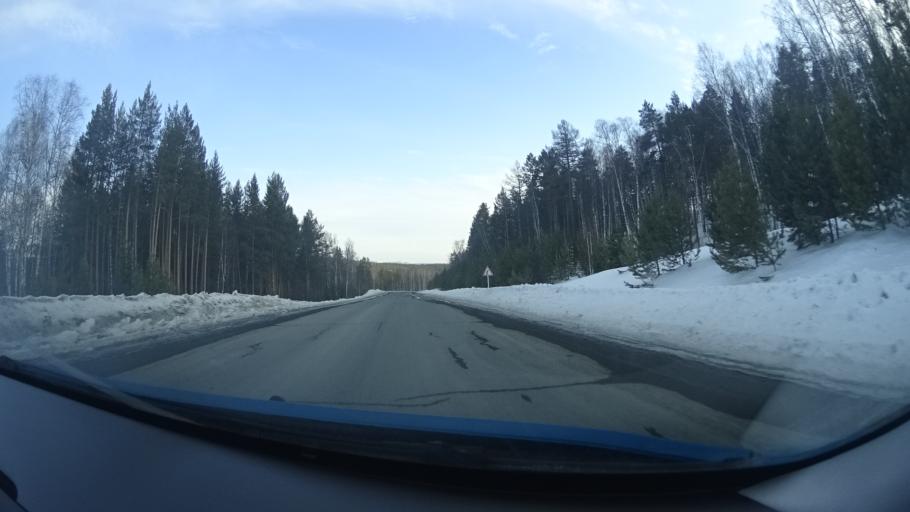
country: RU
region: Bashkortostan
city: Lomovka
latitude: 53.4800
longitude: 58.3150
